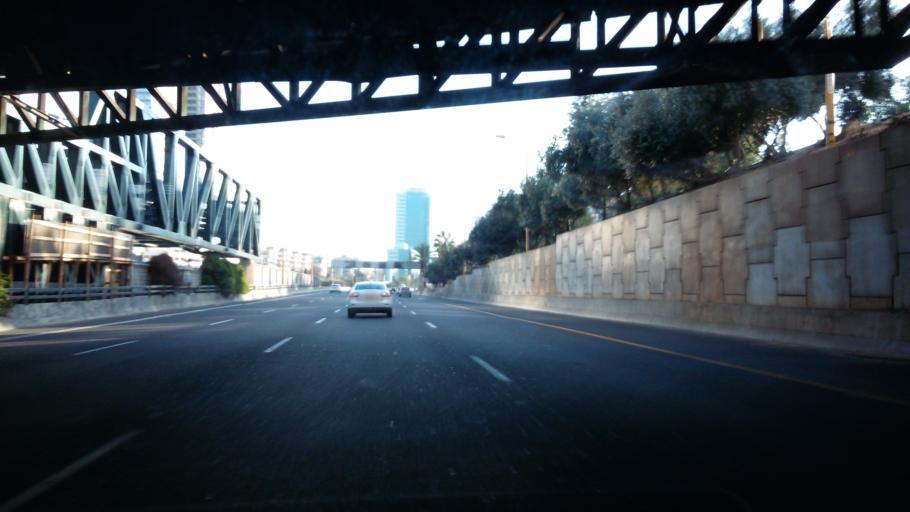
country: IL
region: Tel Aviv
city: Tel Aviv
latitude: 32.0758
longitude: 34.7940
